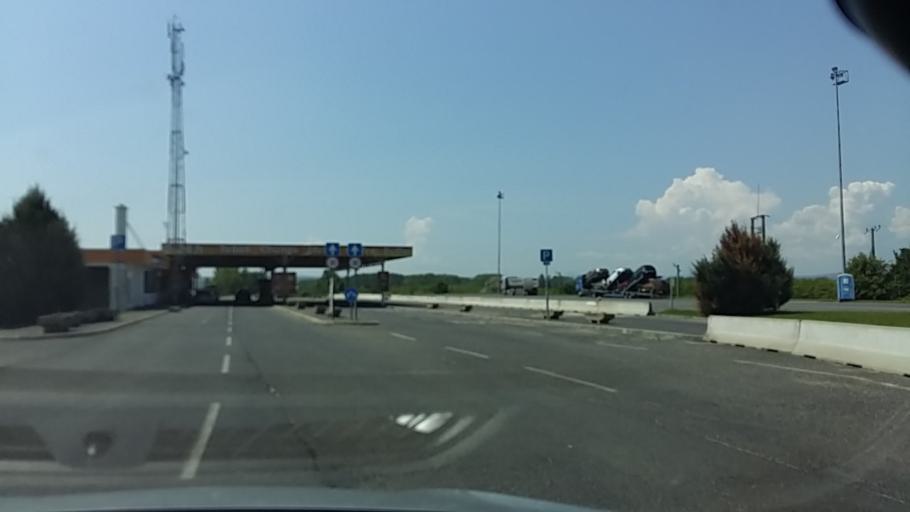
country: AT
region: Burgenland
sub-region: Politischer Bezirk Oberpullendorf
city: Deutschkreutz
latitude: 47.6302
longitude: 16.6277
